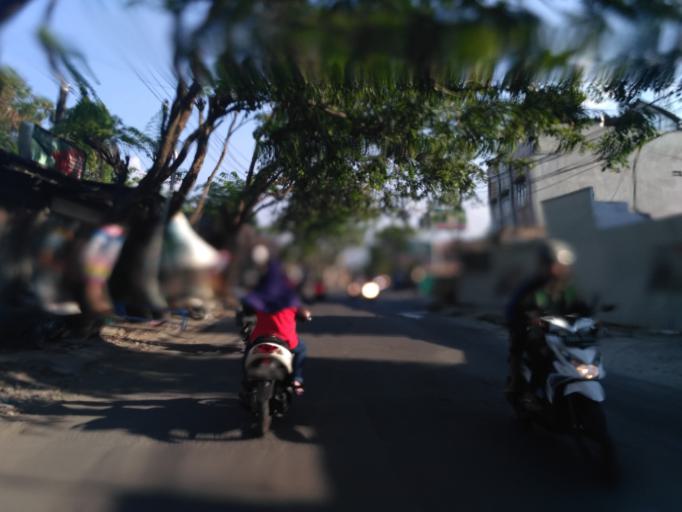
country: ID
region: Central Java
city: Semarang
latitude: -6.9914
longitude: 110.4477
